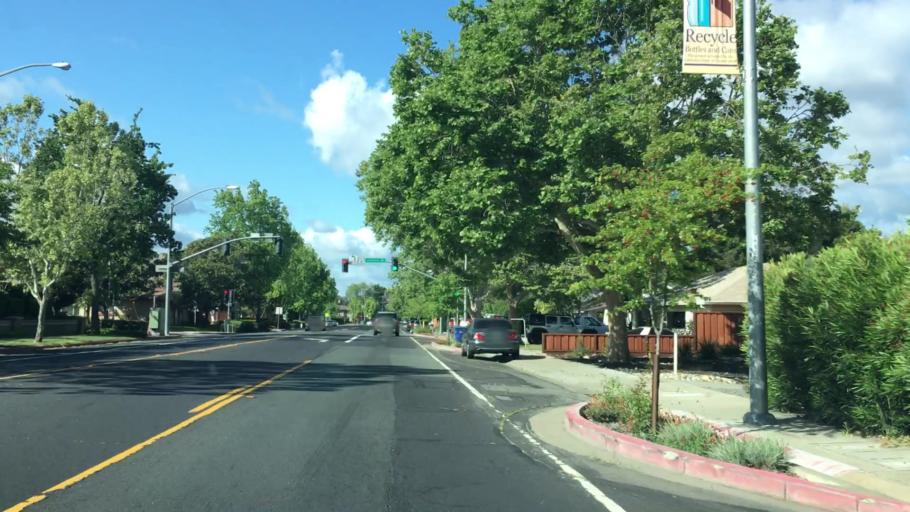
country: US
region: California
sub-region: Contra Costa County
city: Concord
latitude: 37.9905
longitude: -122.0052
